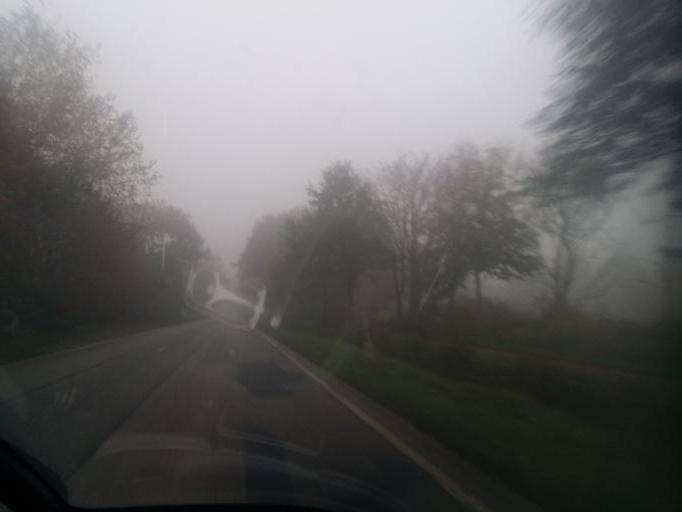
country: DE
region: Schleswig-Holstein
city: Olderup
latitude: 54.5233
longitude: 9.1323
